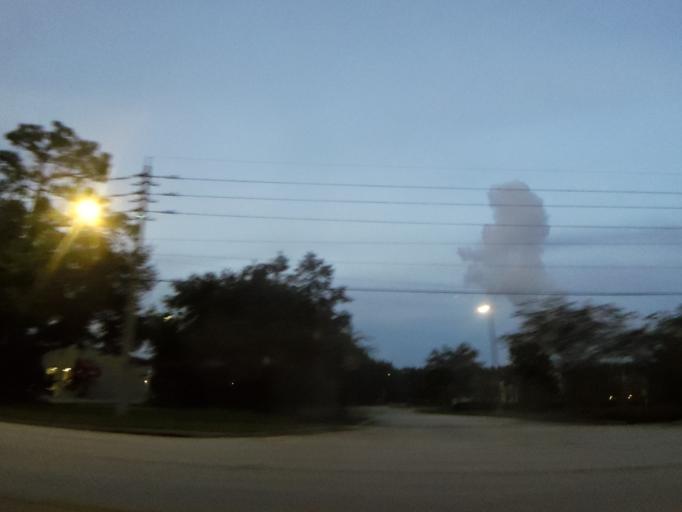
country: US
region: Florida
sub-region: Duval County
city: Jacksonville
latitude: 30.3623
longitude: -81.6063
